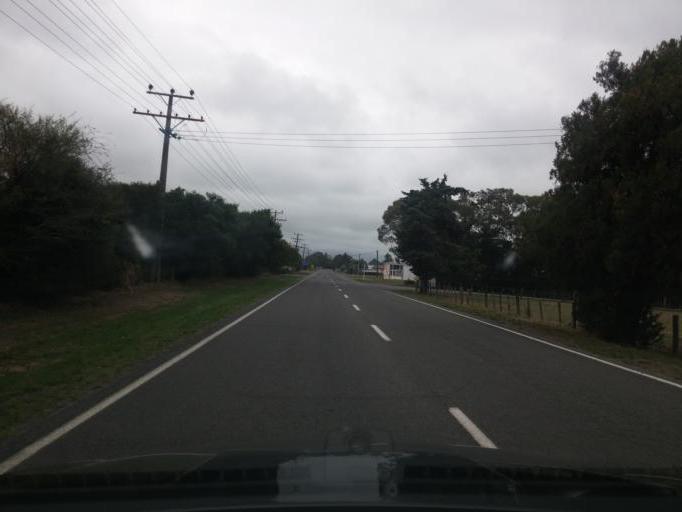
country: NZ
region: Wellington
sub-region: Masterton District
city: Masterton
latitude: -41.0959
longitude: 175.4493
